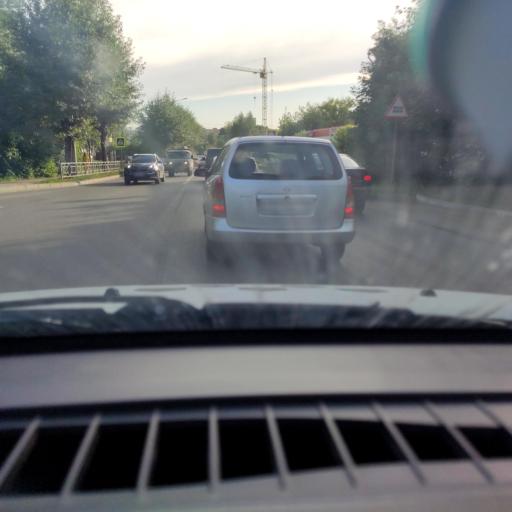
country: RU
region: Kirov
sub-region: Kirovo-Chepetskiy Rayon
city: Kirov
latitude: 58.6217
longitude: 49.6372
